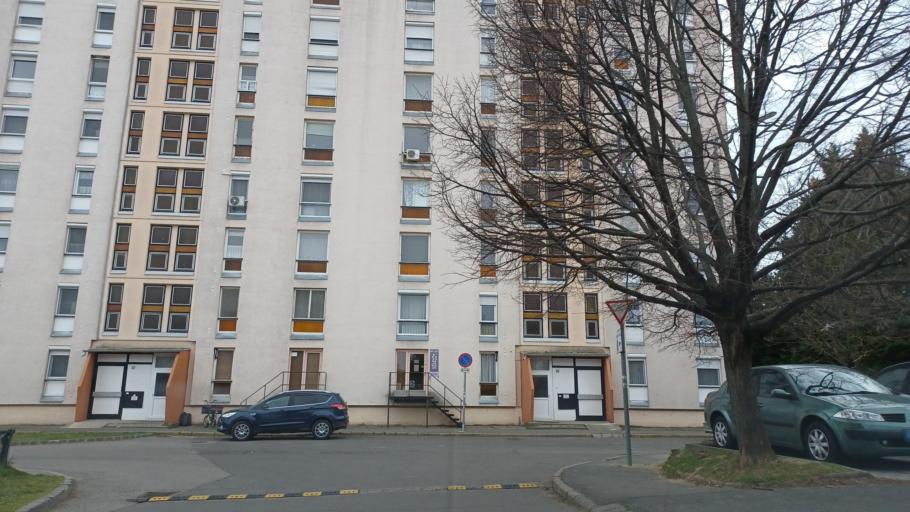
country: HU
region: Tolna
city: Szekszard
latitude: 46.3344
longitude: 18.6995
